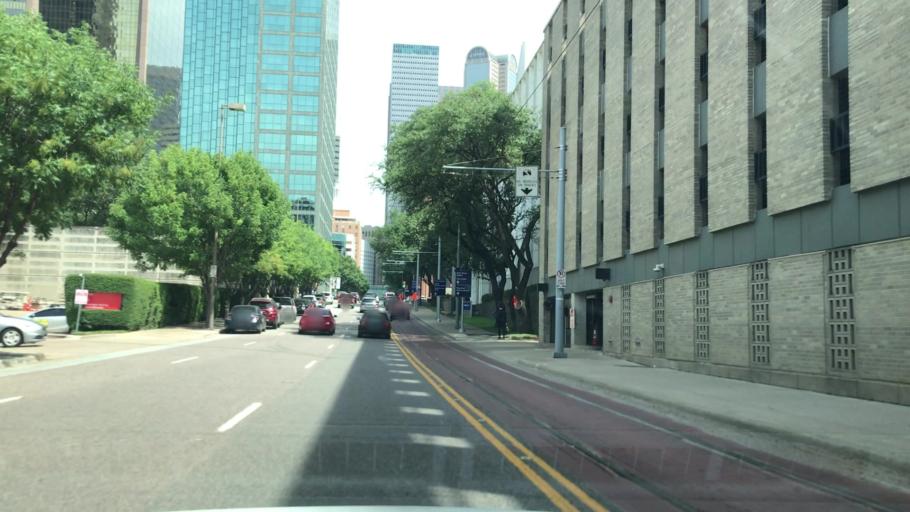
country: US
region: Texas
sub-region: Dallas County
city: Dallas
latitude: 32.7872
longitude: -96.8014
